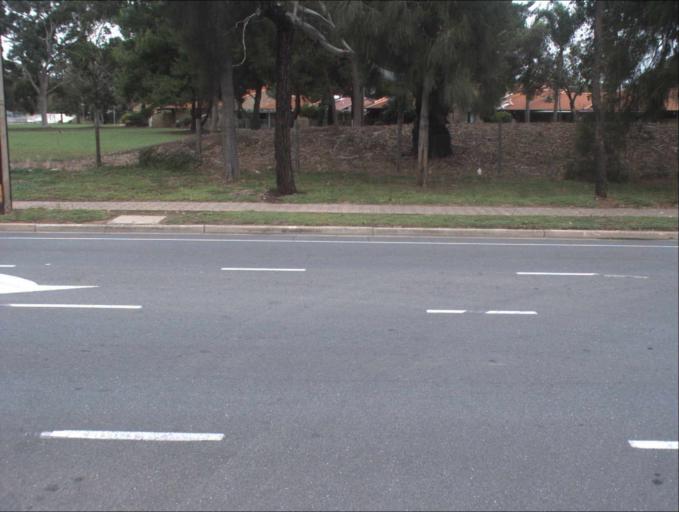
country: AU
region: South Australia
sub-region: Charles Sturt
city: Woodville
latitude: -34.8675
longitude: 138.5656
